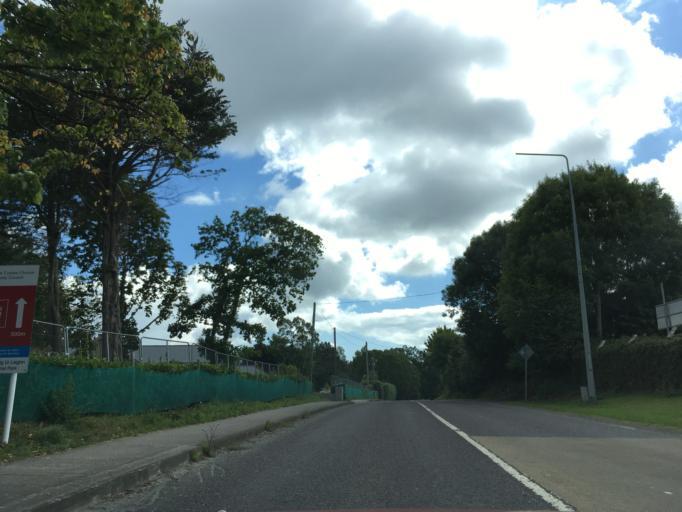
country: IE
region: Munster
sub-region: County Cork
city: Carrigaline
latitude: 51.8120
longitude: -8.3787
